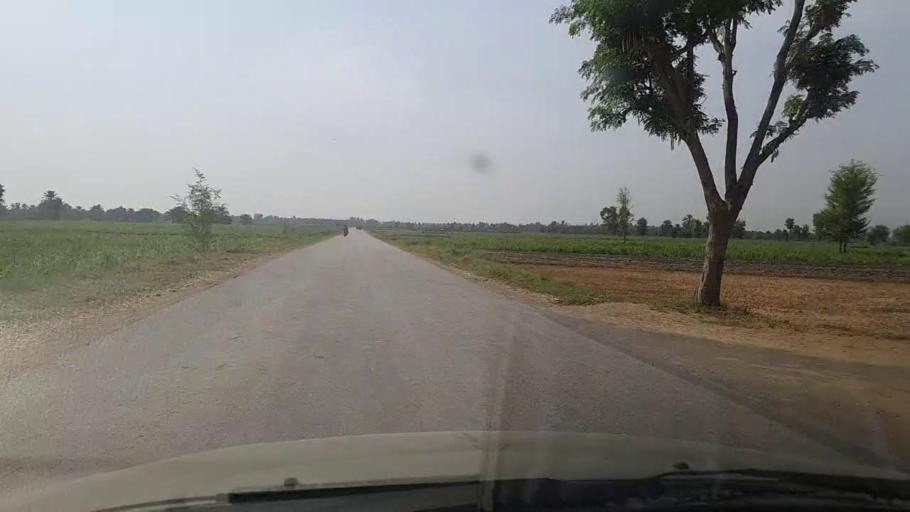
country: PK
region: Sindh
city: Gambat
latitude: 27.4637
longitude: 68.4800
